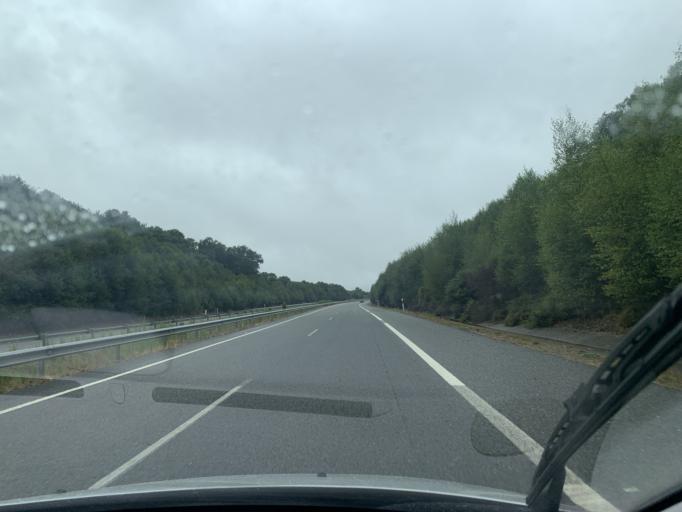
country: ES
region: Galicia
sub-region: Provincia de Lugo
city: Vilalba
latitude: 43.3230
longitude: -7.6489
